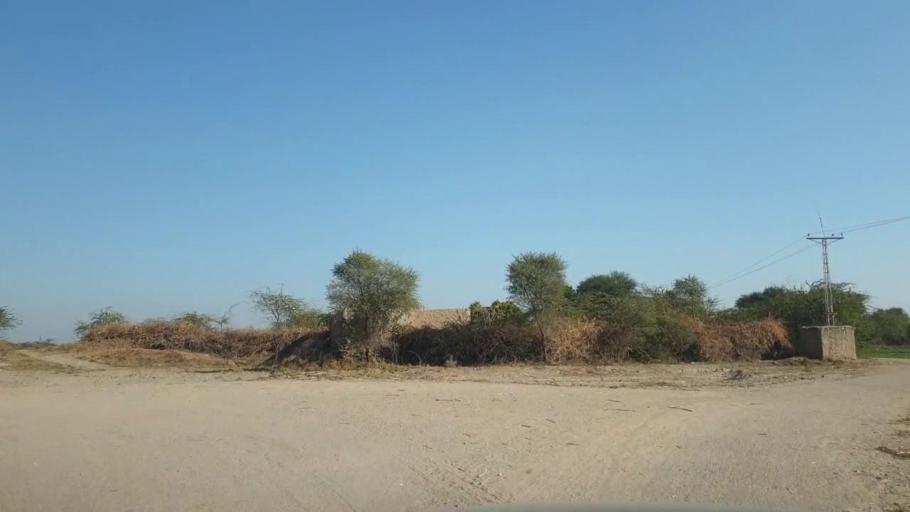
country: PK
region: Sindh
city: Tando Adam
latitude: 25.6853
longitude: 68.6922
